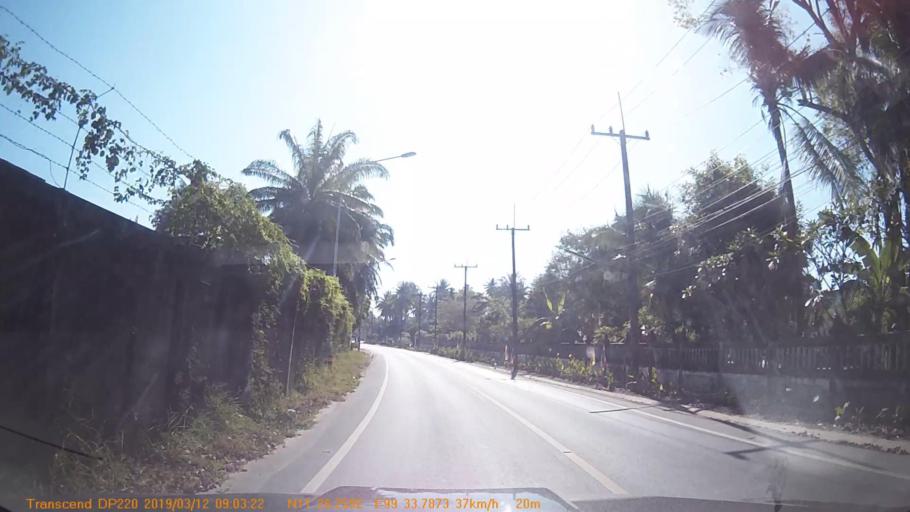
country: TH
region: Prachuap Khiri Khan
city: Thap Sakae
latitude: 11.4376
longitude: 99.5633
